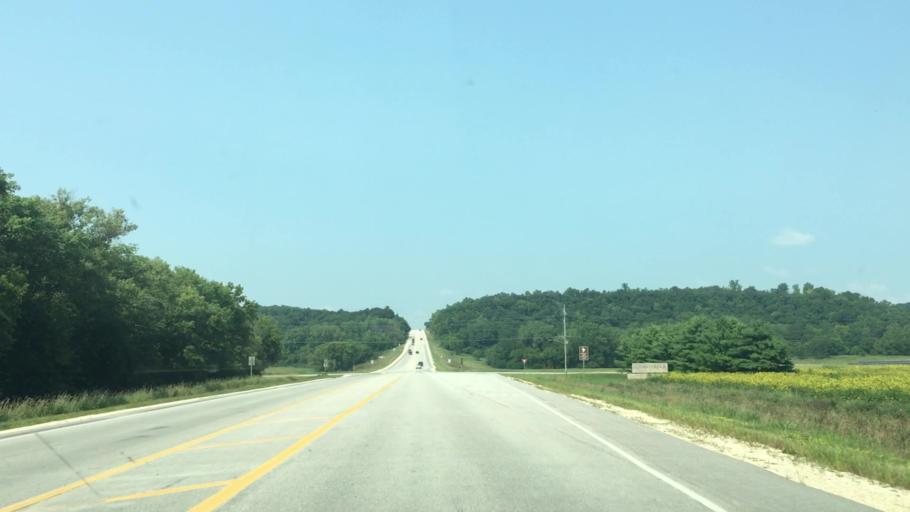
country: US
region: Iowa
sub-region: Winneshiek County
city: Decorah
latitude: 43.3185
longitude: -91.8140
